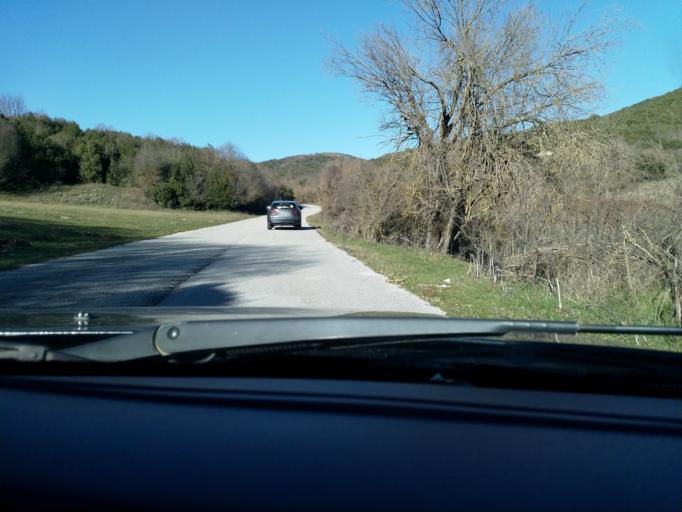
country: GR
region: Epirus
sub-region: Nomos Ioanninon
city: Kalpaki
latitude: 39.8960
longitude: 20.6710
